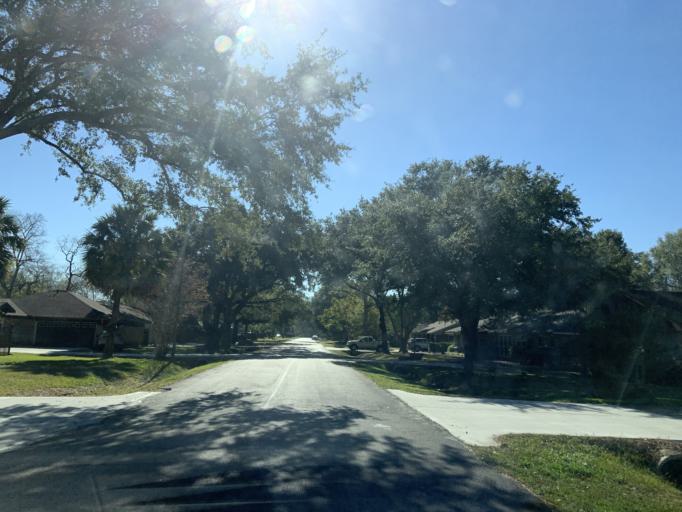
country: US
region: Texas
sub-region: Harris County
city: Bellaire
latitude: 29.6811
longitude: -95.5118
